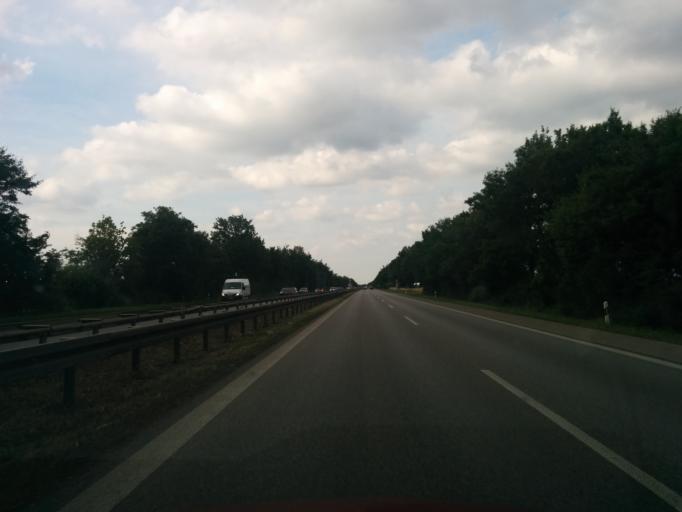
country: DE
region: Bavaria
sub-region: Swabia
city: Konigsbrunn
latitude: 48.2956
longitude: 10.8775
